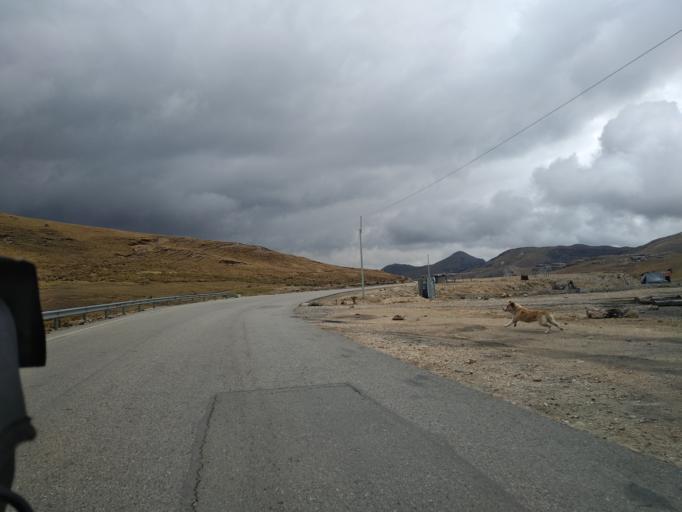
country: PE
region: La Libertad
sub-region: Provincia de Santiago de Chuco
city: Quiruvilca
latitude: -7.9902
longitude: -78.2787
